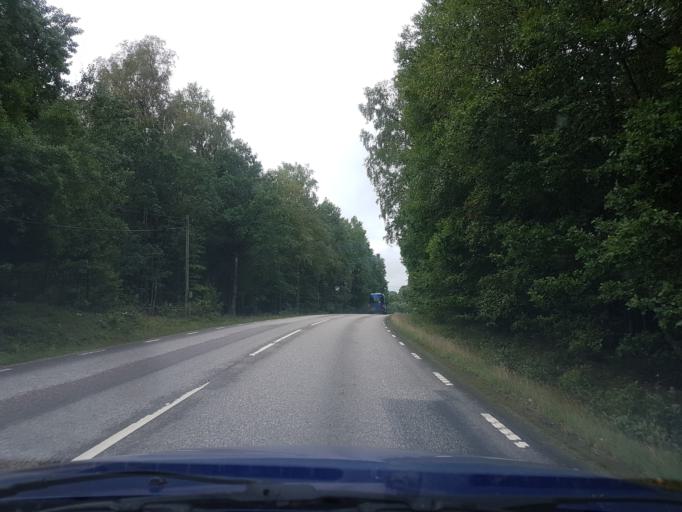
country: SE
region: Vaestra Goetaland
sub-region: Ale Kommun
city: Alvangen
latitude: 57.9389
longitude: 12.1589
